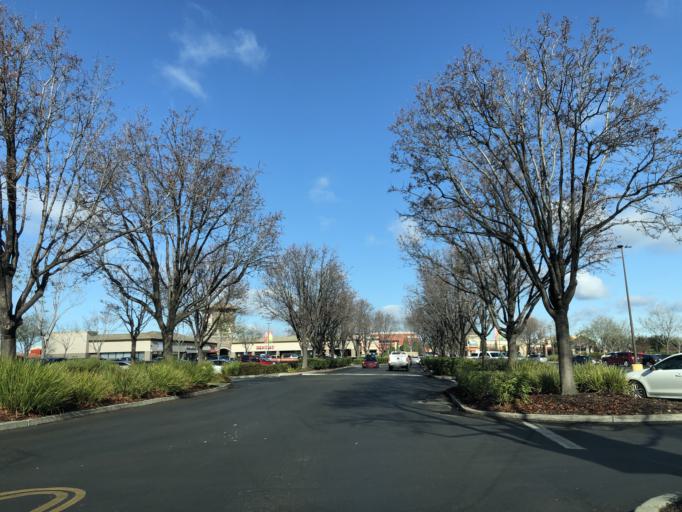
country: US
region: California
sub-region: Contra Costa County
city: Brentwood
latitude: 37.9418
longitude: -121.7380
